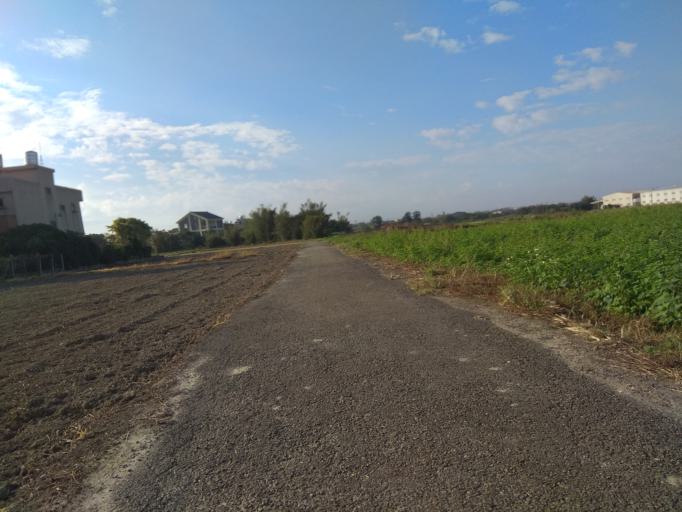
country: TW
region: Taiwan
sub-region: Hsinchu
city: Zhubei
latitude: 24.9790
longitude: 121.0604
